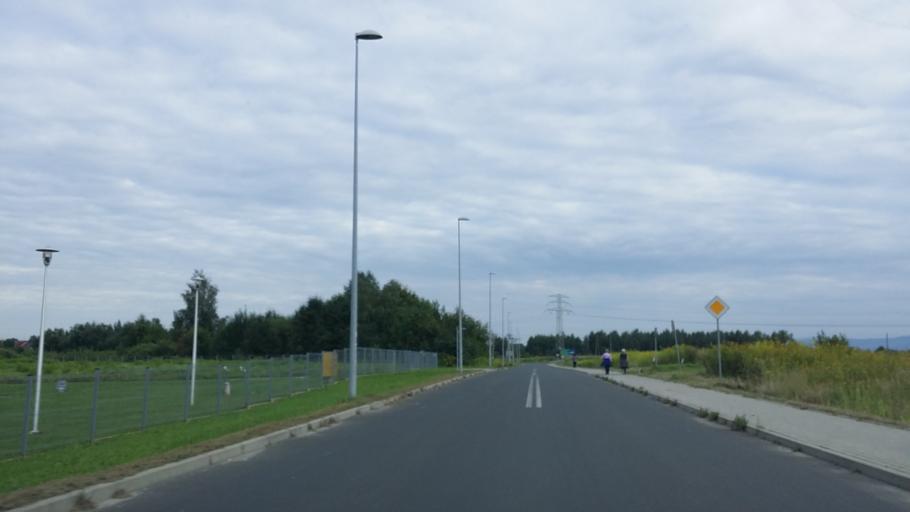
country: PL
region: Lesser Poland Voivodeship
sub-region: Powiat oswiecimski
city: Zator
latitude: 49.9936
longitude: 19.4231
